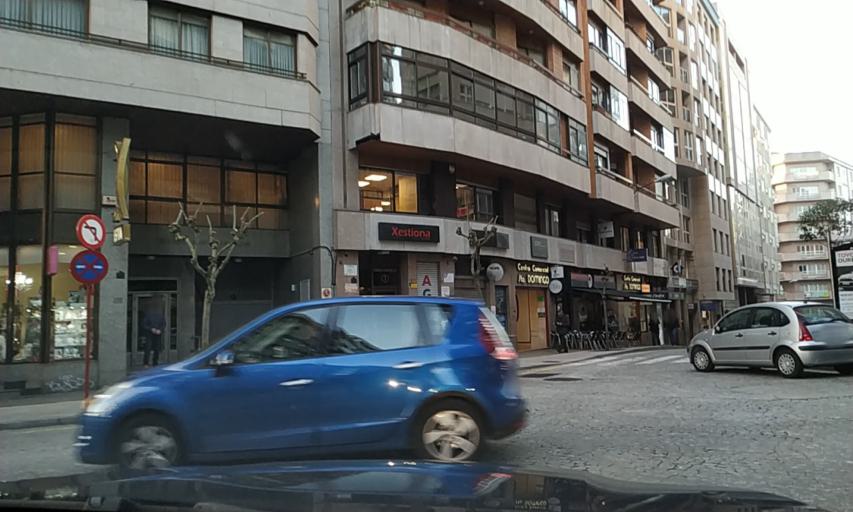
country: ES
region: Galicia
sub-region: Provincia de Ourense
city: Ourense
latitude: 42.3394
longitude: -7.8621
